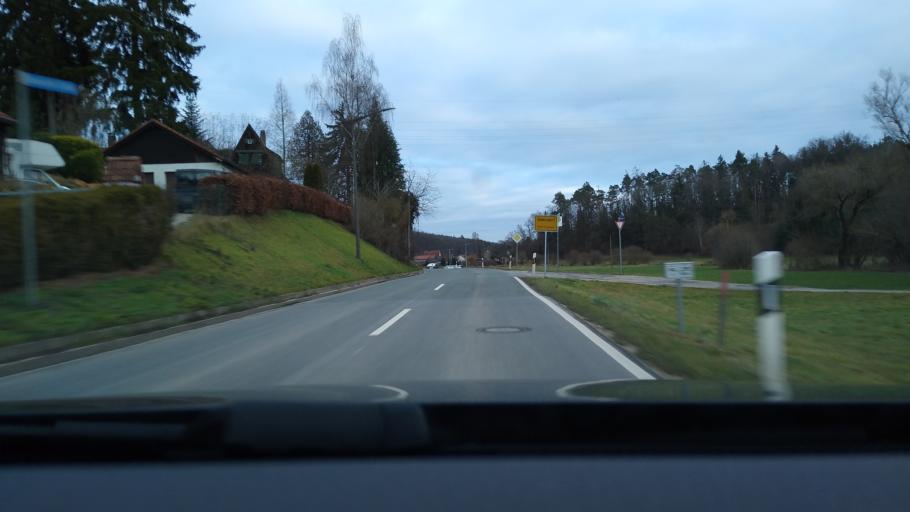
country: DE
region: Bavaria
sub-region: Regierungsbezirk Mittelfranken
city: Schwabach
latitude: 49.3694
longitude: 10.9919
